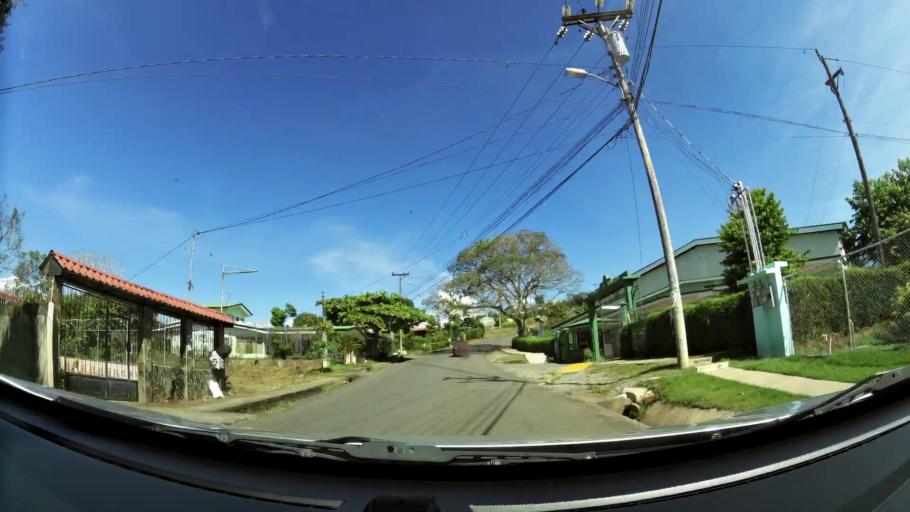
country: CR
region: San Jose
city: San Isidro
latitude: 9.3636
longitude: -83.7128
